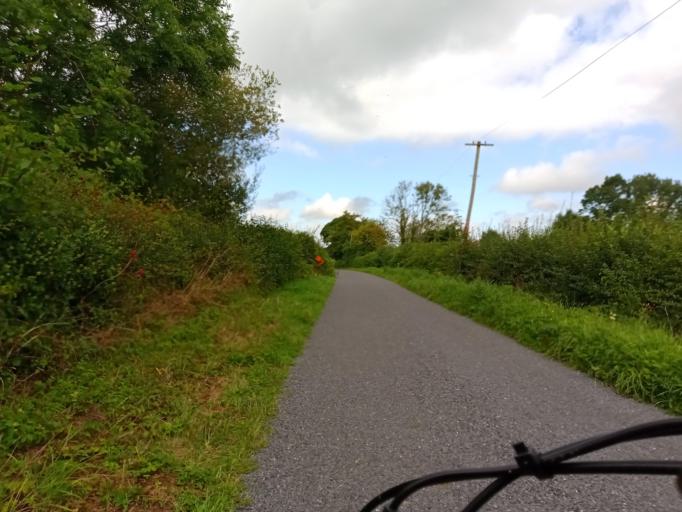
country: IE
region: Leinster
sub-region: Kilkenny
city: Callan
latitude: 52.5344
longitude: -7.2869
